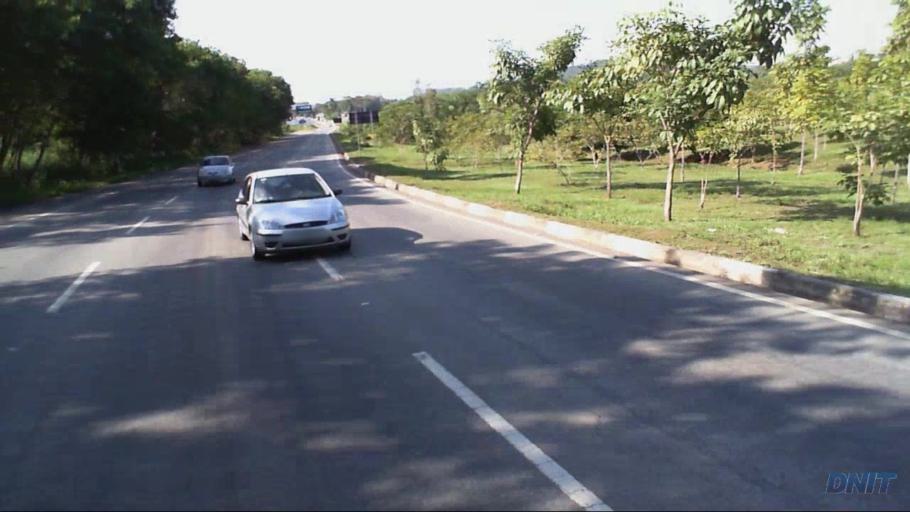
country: BR
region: Minas Gerais
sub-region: Coronel Fabriciano
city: Coronel Fabriciano
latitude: -19.5125
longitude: -42.5759
